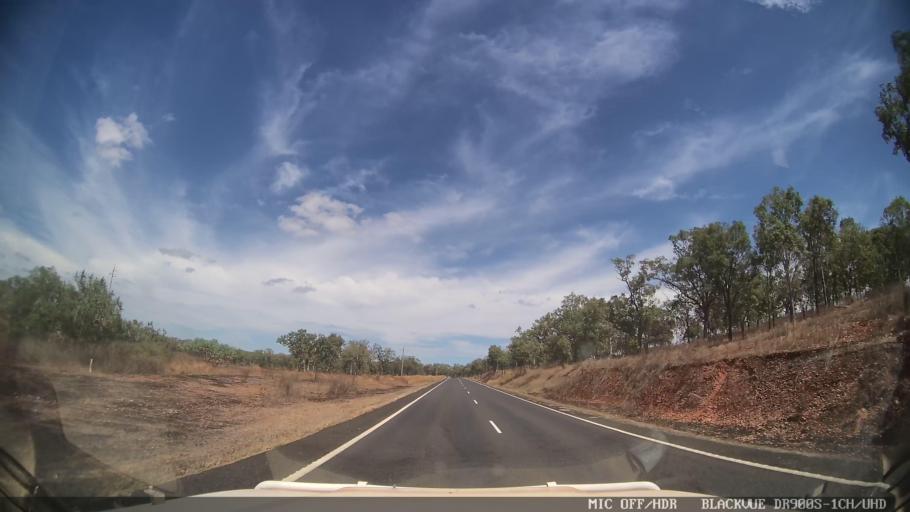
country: AU
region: Queensland
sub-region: Cook
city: Cooktown
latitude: -15.7973
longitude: 144.9257
